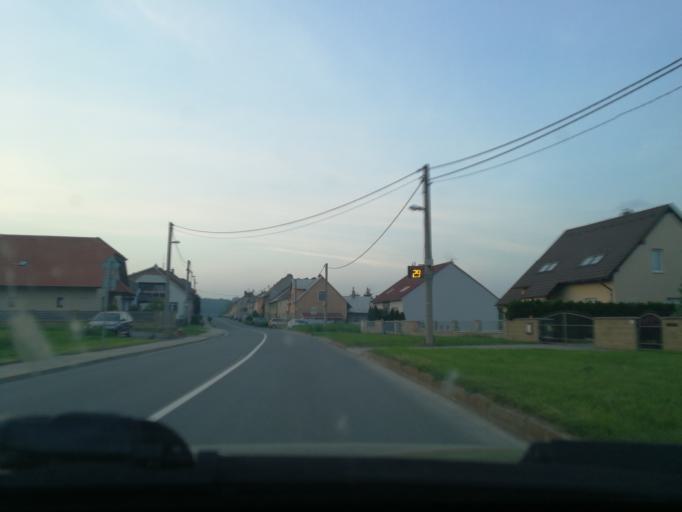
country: CZ
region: Zlin
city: Tlumacov
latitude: 49.2714
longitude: 17.5500
